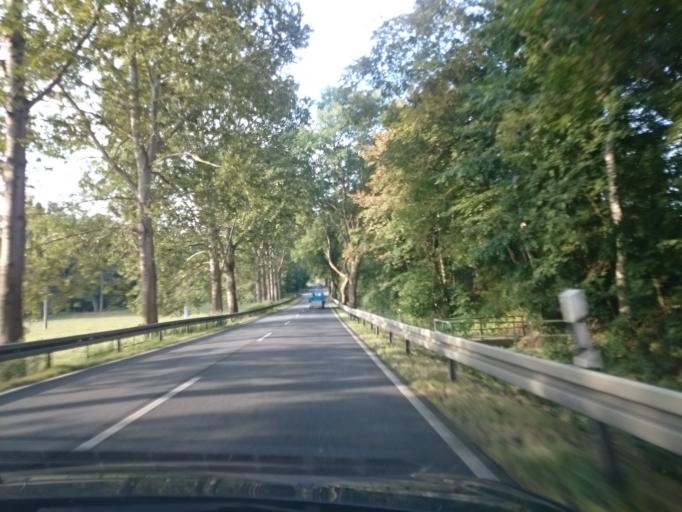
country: DE
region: Mecklenburg-Vorpommern
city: Demmin
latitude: 53.8666
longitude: 13.0130
